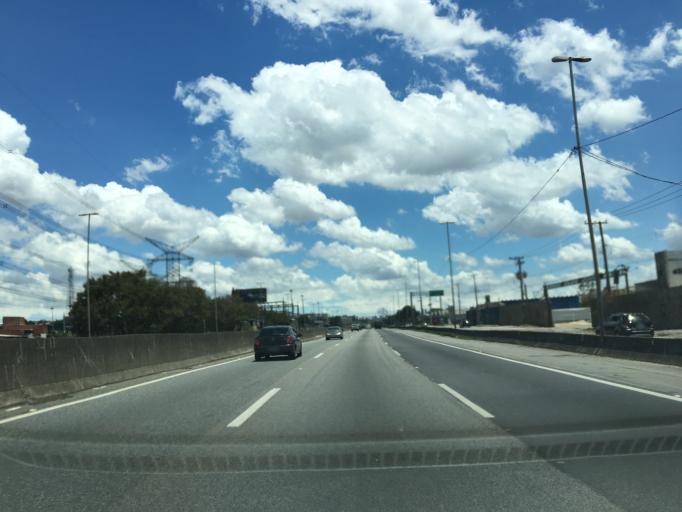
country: BR
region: Sao Paulo
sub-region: Guarulhos
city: Guarulhos
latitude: -23.4778
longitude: -46.5602
